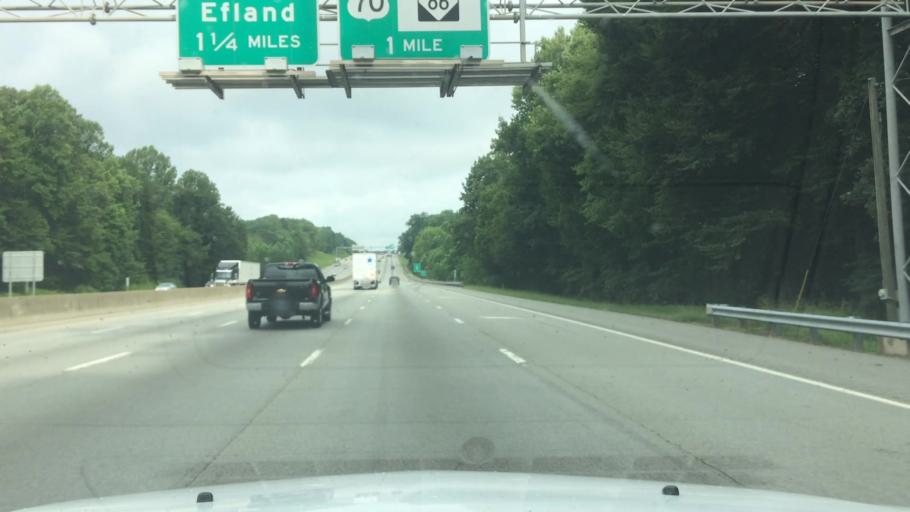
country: US
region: North Carolina
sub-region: Orange County
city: Hillsborough
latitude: 36.0648
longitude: -79.1414
